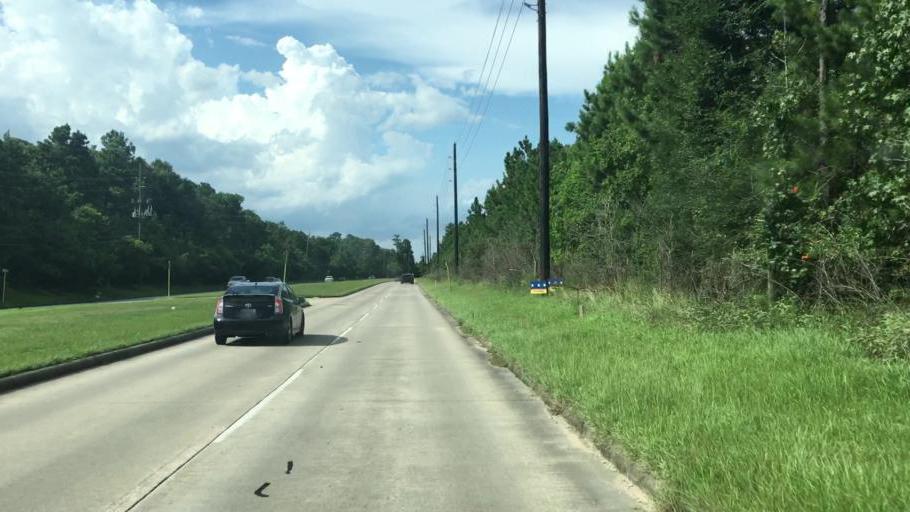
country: US
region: Texas
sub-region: Harris County
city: Atascocita
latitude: 29.9494
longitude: -95.1745
